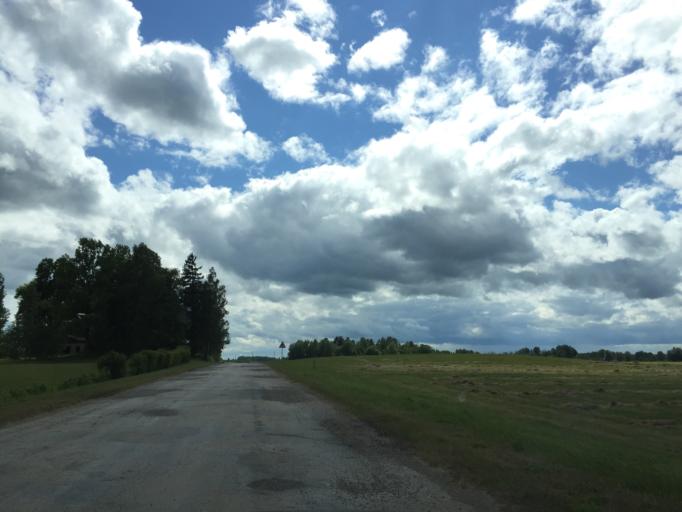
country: LV
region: Lecava
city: Iecava
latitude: 56.5227
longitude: 24.3511
